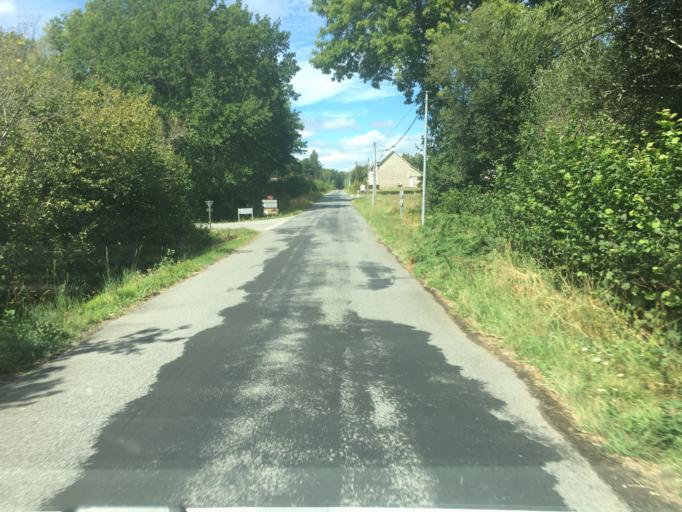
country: FR
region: Auvergne
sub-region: Departement du Cantal
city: Champagnac
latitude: 45.4241
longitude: 2.3761
